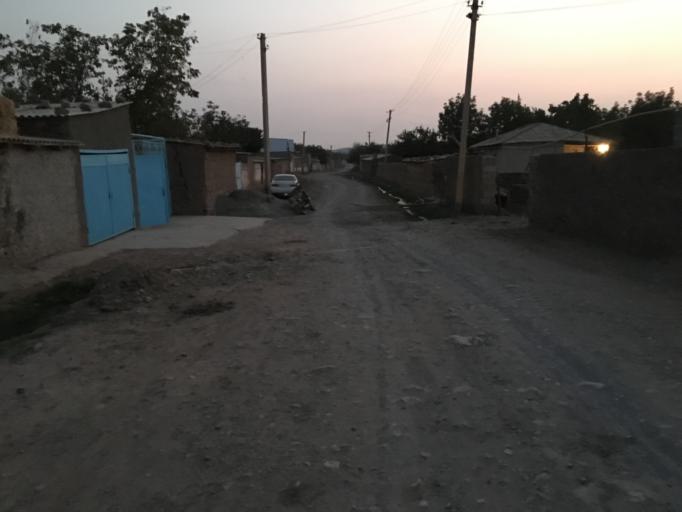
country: UZ
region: Qashqadaryo
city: Qorashina
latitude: 37.9181
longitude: 66.4822
